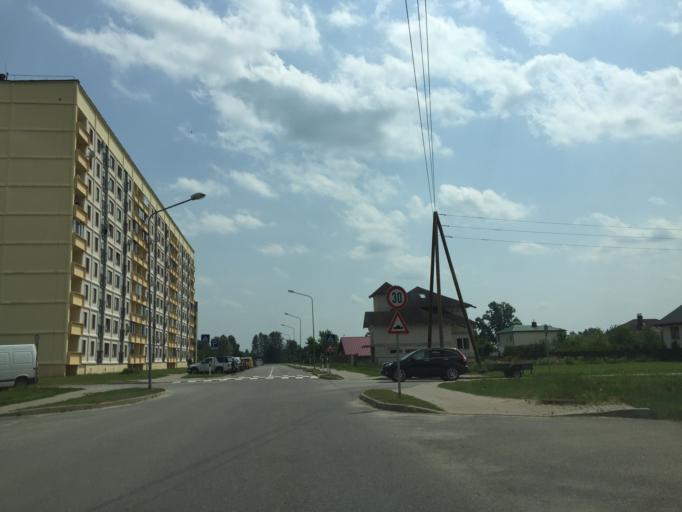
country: LV
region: Olaine
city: Olaine
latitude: 56.7792
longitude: 23.9227
